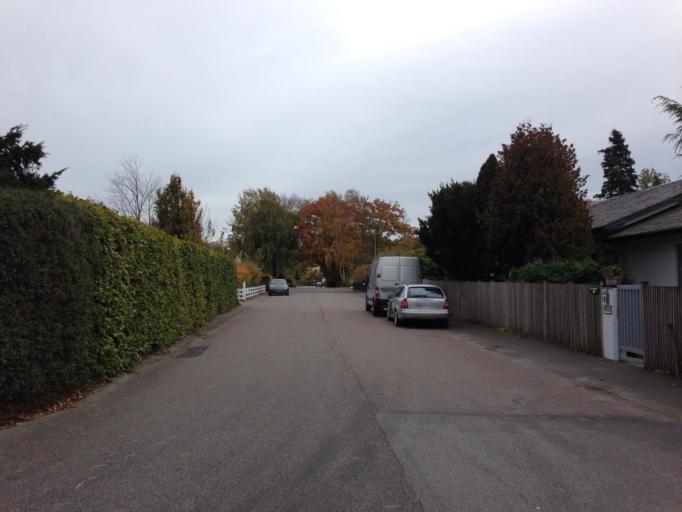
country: SE
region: Skane
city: Bjarred
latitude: 55.7158
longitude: 13.0225
